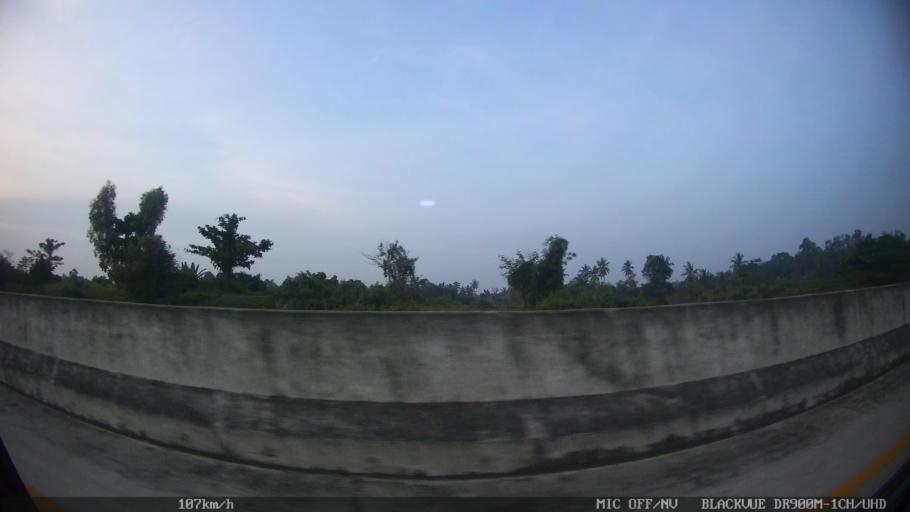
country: ID
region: Lampung
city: Pasuruan
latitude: -5.7317
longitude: 105.6801
